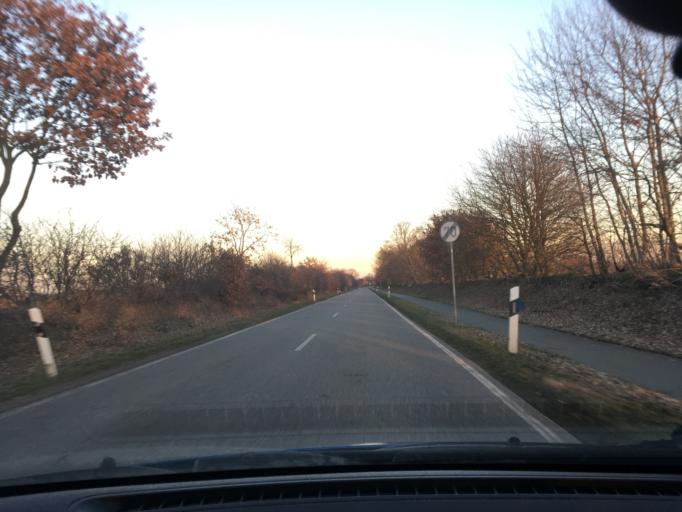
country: DE
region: Schleswig-Holstein
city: Brothen
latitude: 53.4798
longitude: 10.6518
